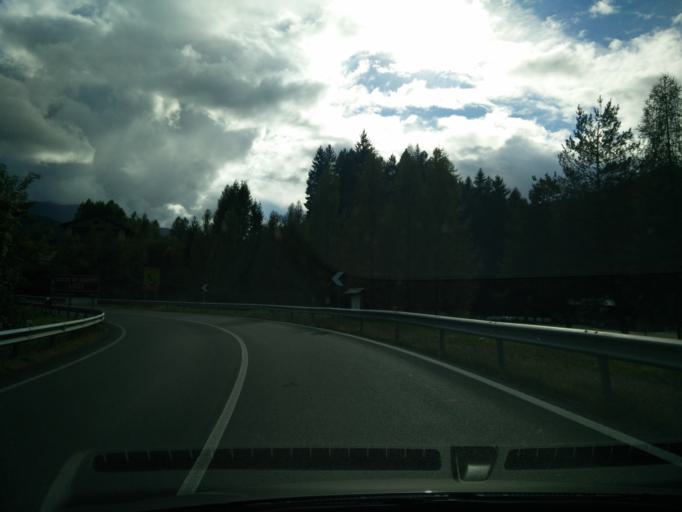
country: IT
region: Veneto
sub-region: Provincia di Belluno
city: Lozzo di Cadore
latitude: 46.4729
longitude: 12.4321
